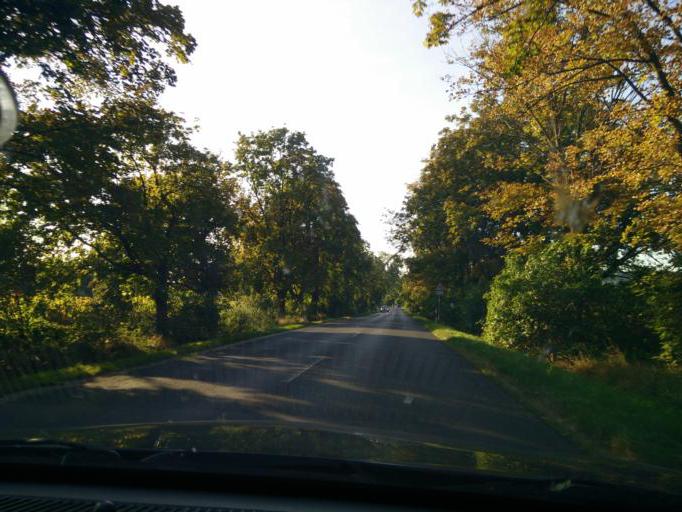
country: HU
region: Pest
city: Zsambek
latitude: 47.5345
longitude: 18.7279
